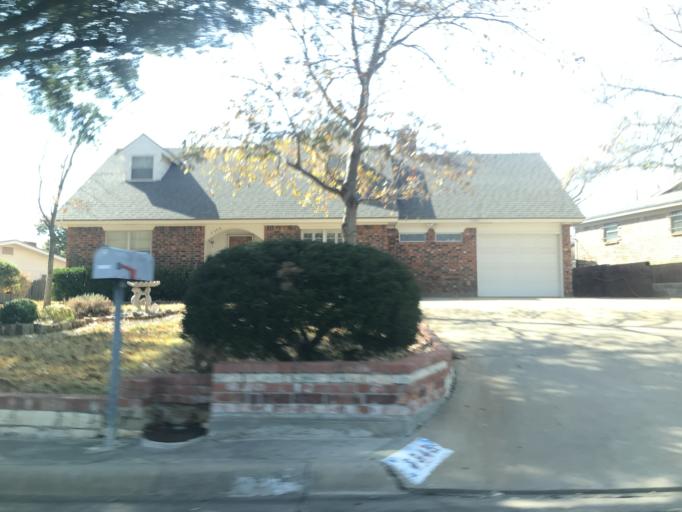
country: US
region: Texas
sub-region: Tom Green County
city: San Angelo
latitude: 31.4422
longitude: -100.4787
